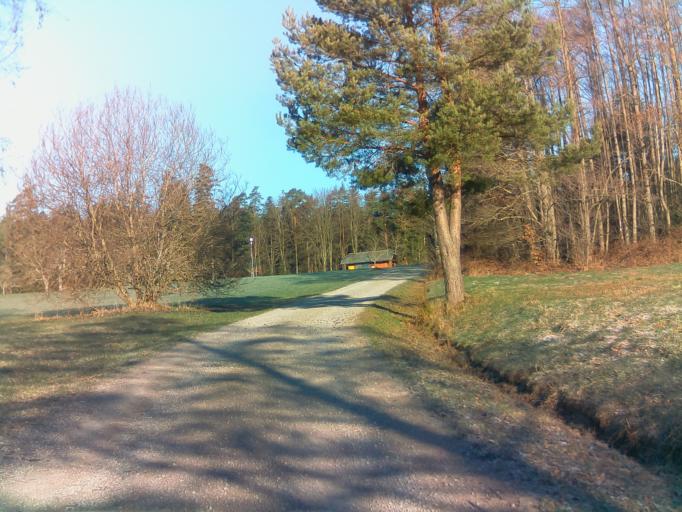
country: DE
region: Baden-Wuerttemberg
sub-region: Karlsruhe Region
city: Oberreichenbach
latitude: 48.7379
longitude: 8.6578
